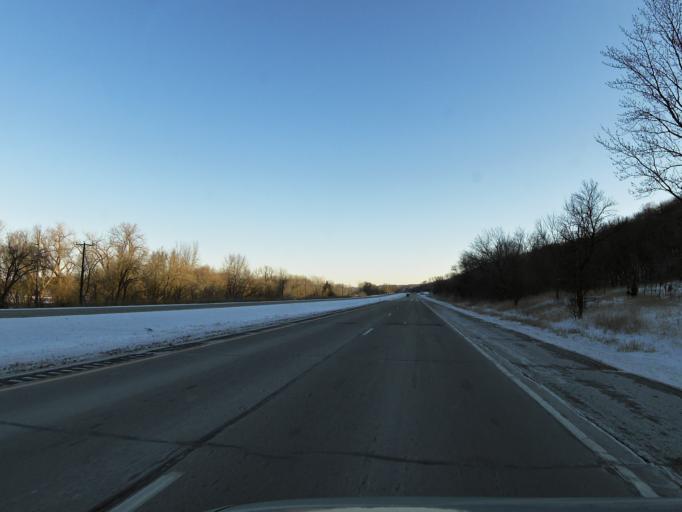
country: US
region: Minnesota
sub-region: Scott County
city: Jordan
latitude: 44.6843
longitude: -93.6149
